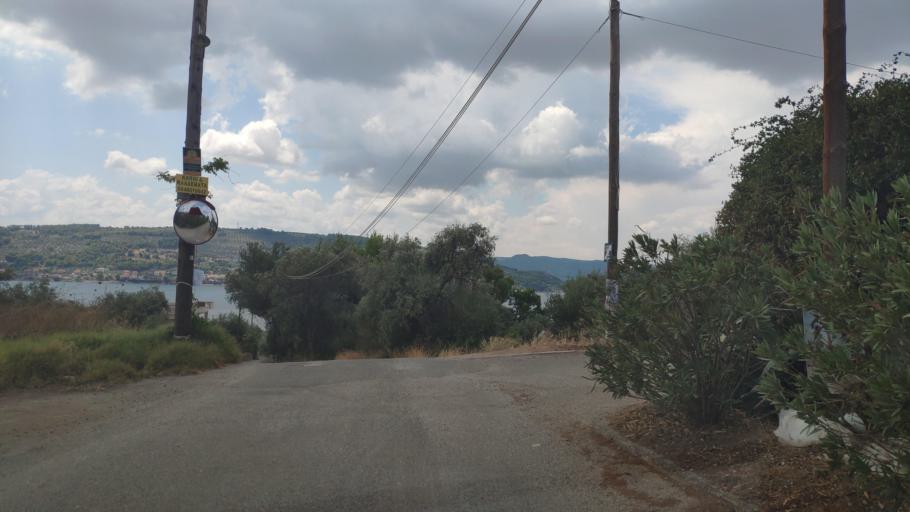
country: GR
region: Central Greece
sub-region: Nomos Fthiotidos
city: Malesina
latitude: 38.6658
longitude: 23.1817
